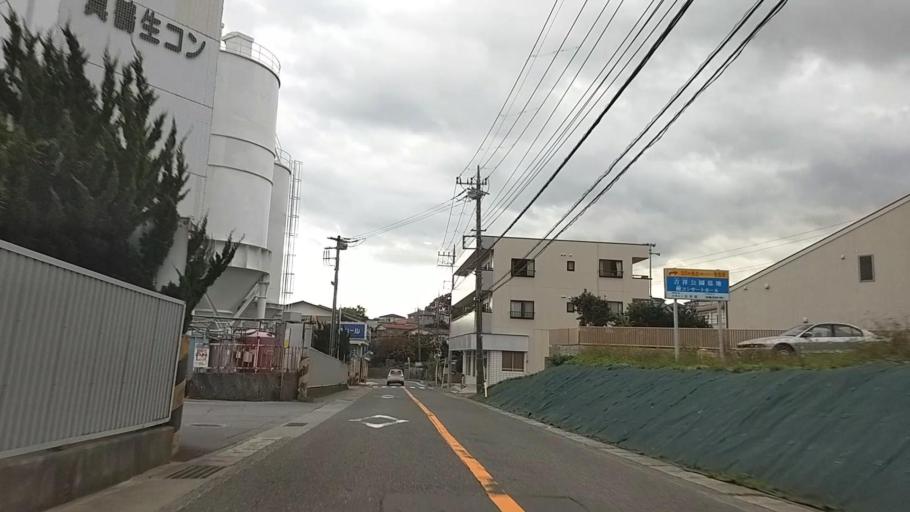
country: JP
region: Kanagawa
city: Yugawara
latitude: 35.1604
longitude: 139.1317
